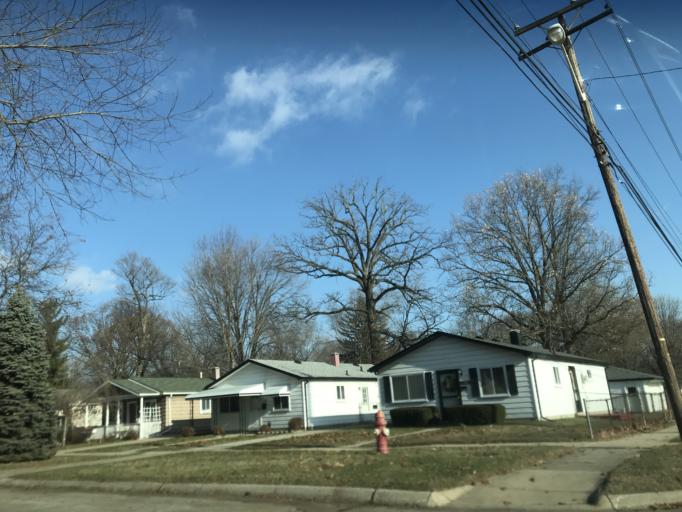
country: US
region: Michigan
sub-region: Oakland County
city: Madison Heights
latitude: 42.4965
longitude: -83.1152
